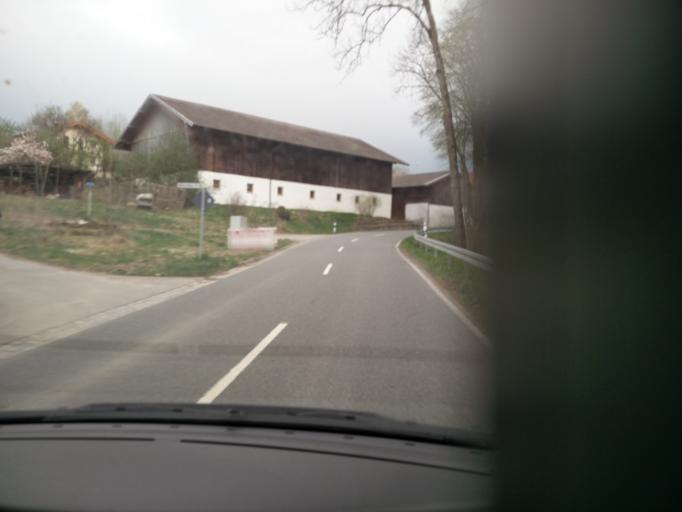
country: DE
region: Bavaria
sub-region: Upper Bavaria
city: Amerang
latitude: 47.9776
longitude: 12.2970
